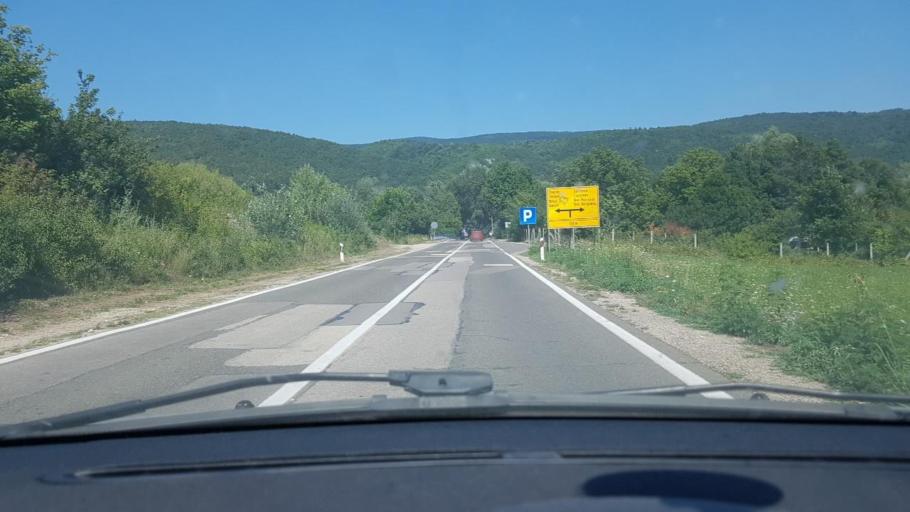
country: BA
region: Federation of Bosnia and Herzegovina
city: Bihac
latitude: 44.7715
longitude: 15.9464
